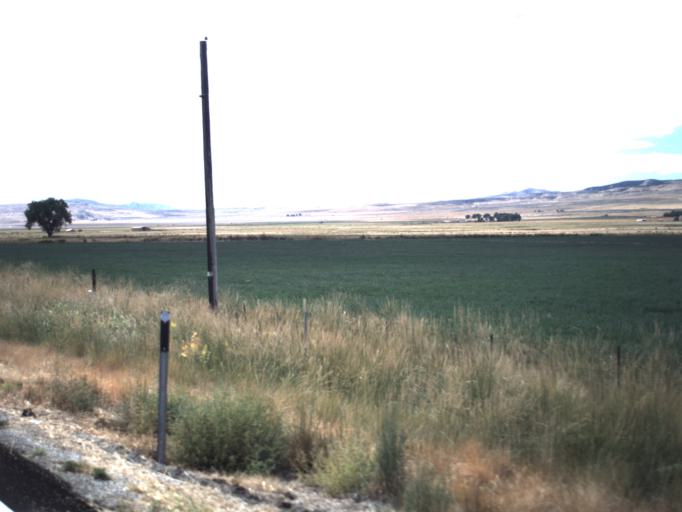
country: US
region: Utah
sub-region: Box Elder County
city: Garland
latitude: 41.7789
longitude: -112.4353
